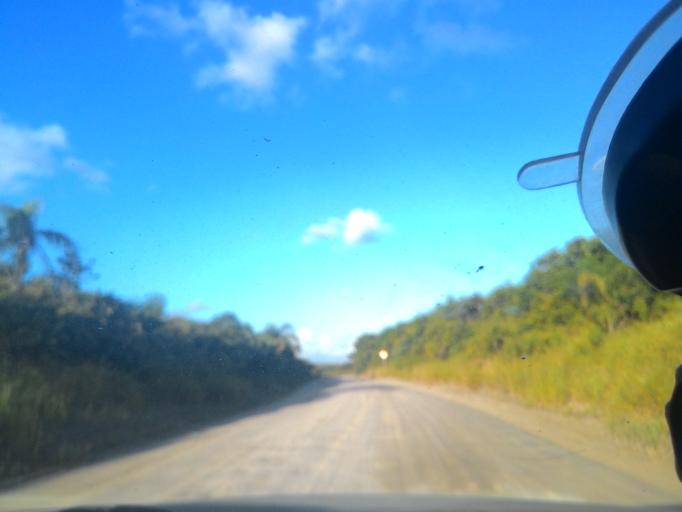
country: BR
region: Sao Paulo
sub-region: Pariquera-Acu
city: Pariquera Acu
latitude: -24.8762
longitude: -47.7319
